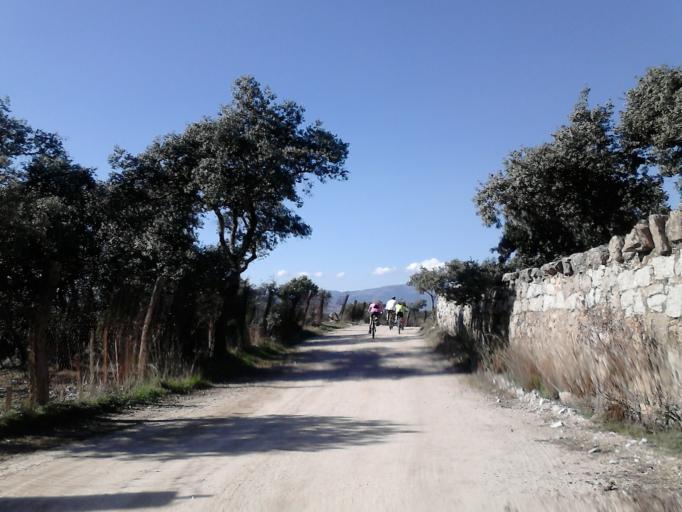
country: ES
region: Madrid
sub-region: Provincia de Madrid
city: Galapagar
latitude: 40.5604
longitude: -3.9888
